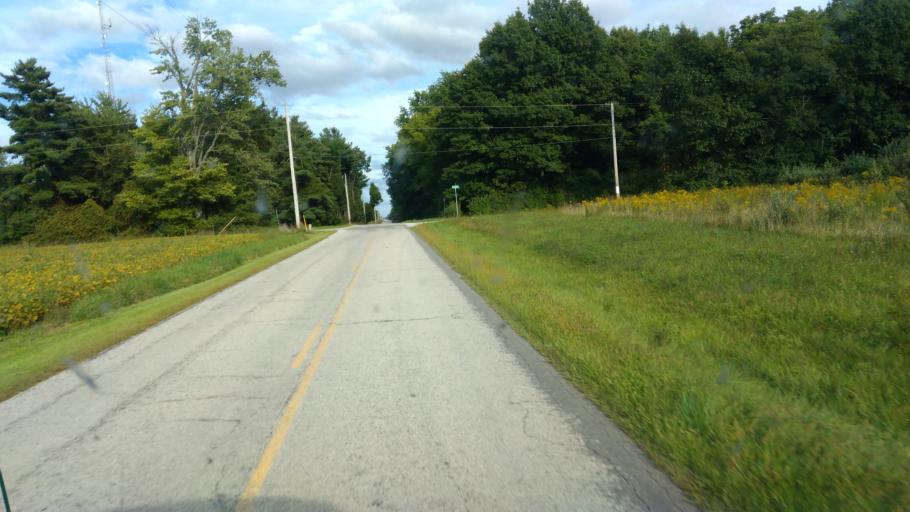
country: US
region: Ohio
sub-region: Crawford County
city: Bucyrus
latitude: 40.9212
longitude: -82.9983
